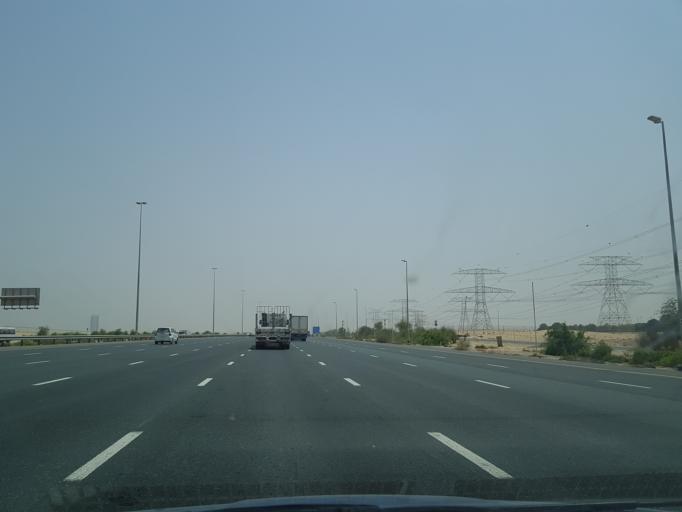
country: AE
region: Dubai
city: Dubai
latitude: 25.0516
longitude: 55.3115
